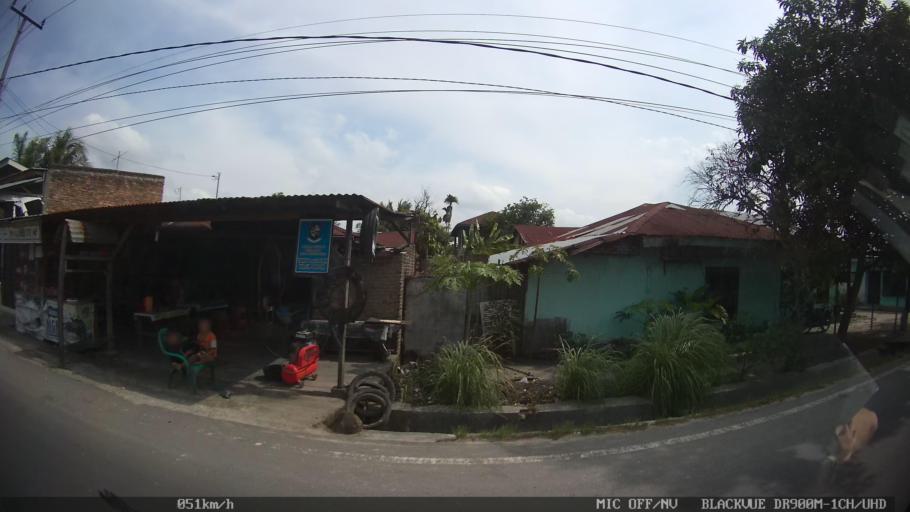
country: ID
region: North Sumatra
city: Percut
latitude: 3.6114
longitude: 98.8229
